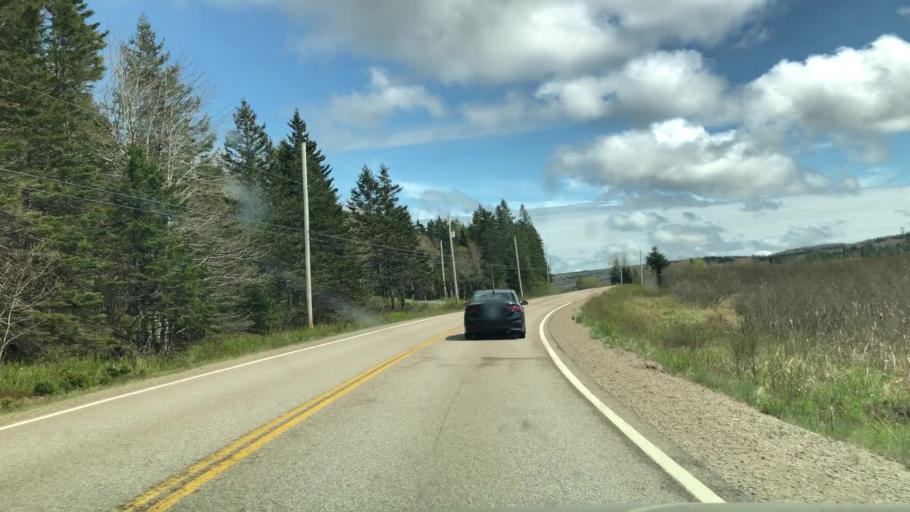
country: CA
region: Nova Scotia
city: Antigonish
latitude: 45.1904
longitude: -61.9898
